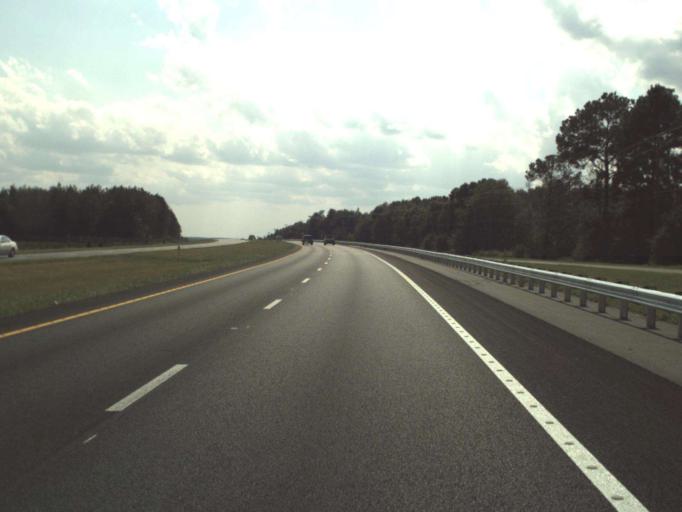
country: US
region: Florida
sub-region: Holmes County
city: Bonifay
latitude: 30.5414
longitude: -85.8329
